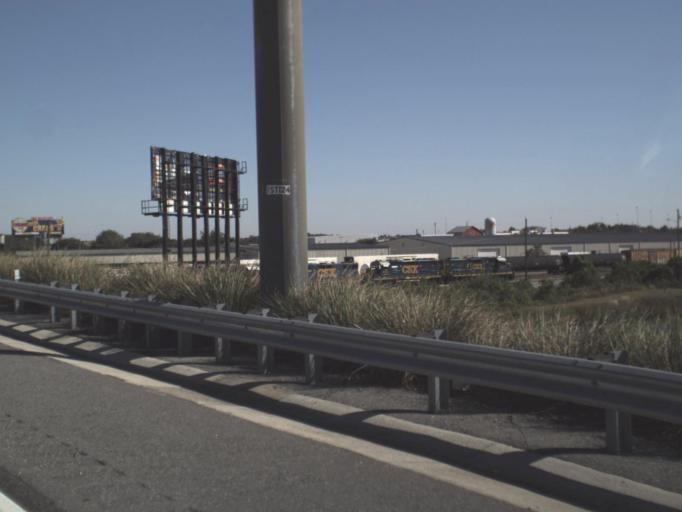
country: US
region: Florida
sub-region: Orange County
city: Belle Isle
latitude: 28.4458
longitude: -81.3685
